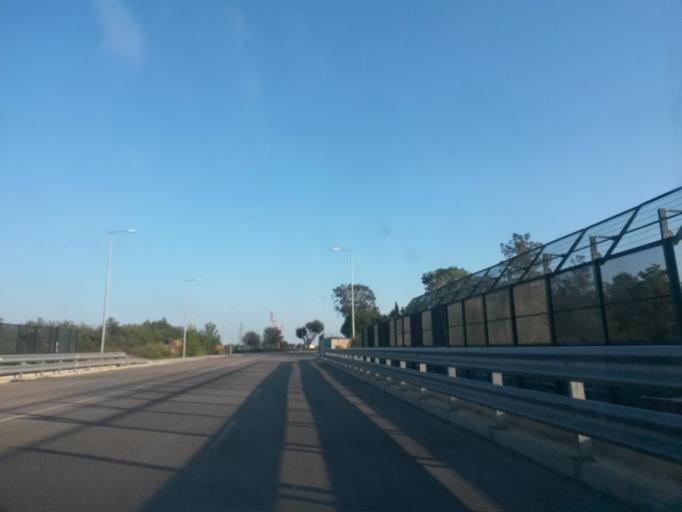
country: ES
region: Catalonia
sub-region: Provincia de Girona
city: Fornells de la Selva
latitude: 41.9444
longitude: 2.7997
